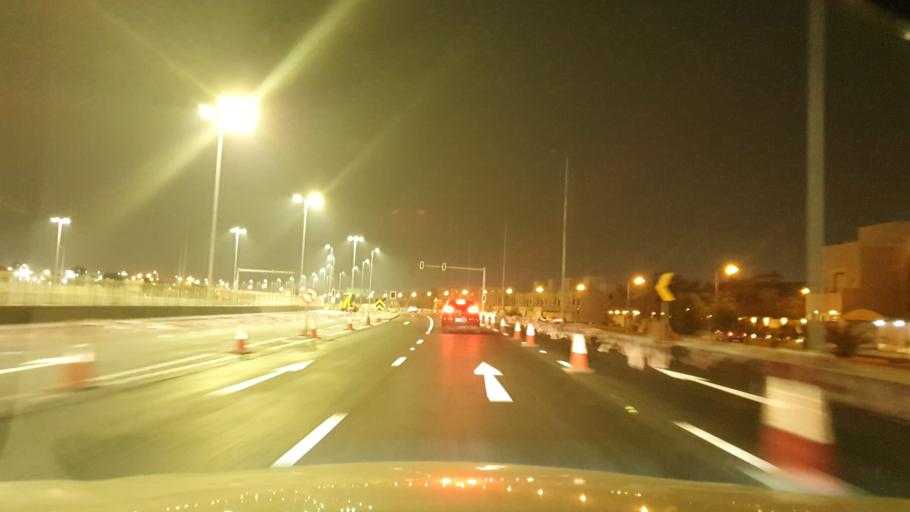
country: BH
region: Northern
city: Madinat `Isa
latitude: 26.1574
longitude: 50.5542
